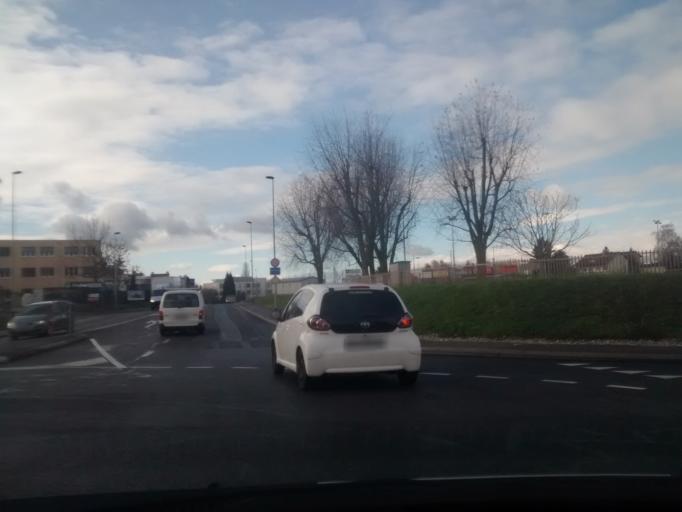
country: CH
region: Vaud
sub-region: Lausanne District
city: Cheseaux
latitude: 46.5827
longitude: 6.6005
